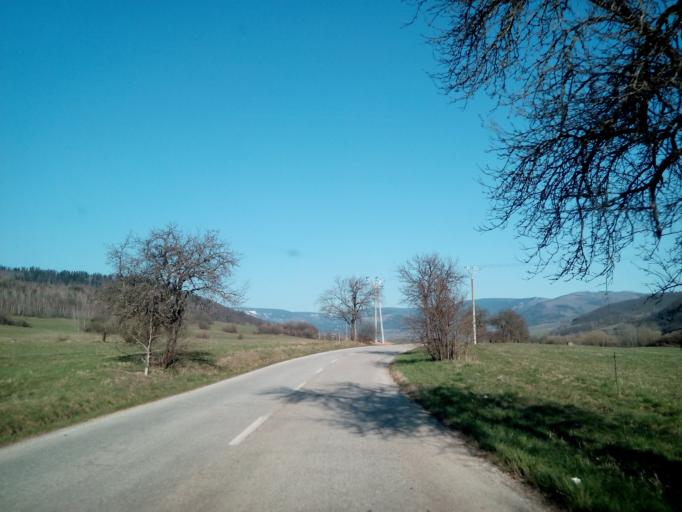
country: SK
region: Kosicky
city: Dobsina
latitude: 48.6873
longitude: 20.3233
